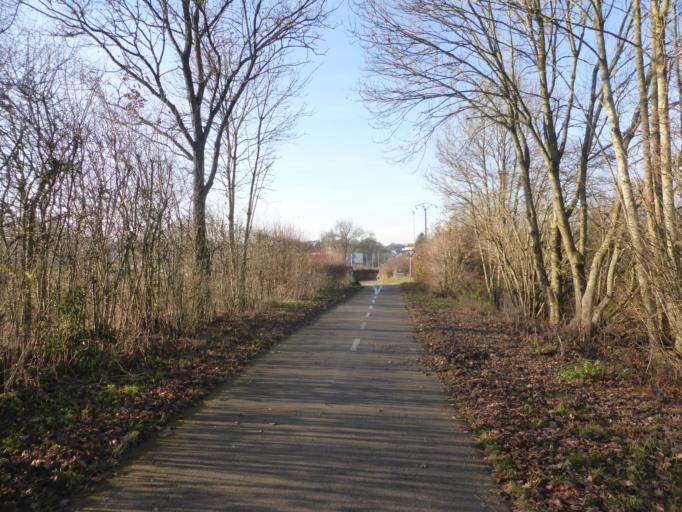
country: LU
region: Luxembourg
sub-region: Canton de Capellen
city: Clemency
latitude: 49.5938
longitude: 5.8849
